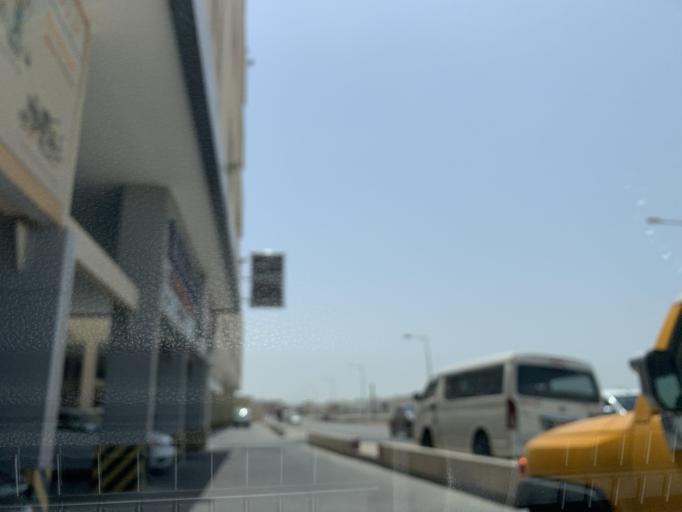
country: BH
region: Northern
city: Madinat `Isa
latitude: 26.1944
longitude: 50.5438
